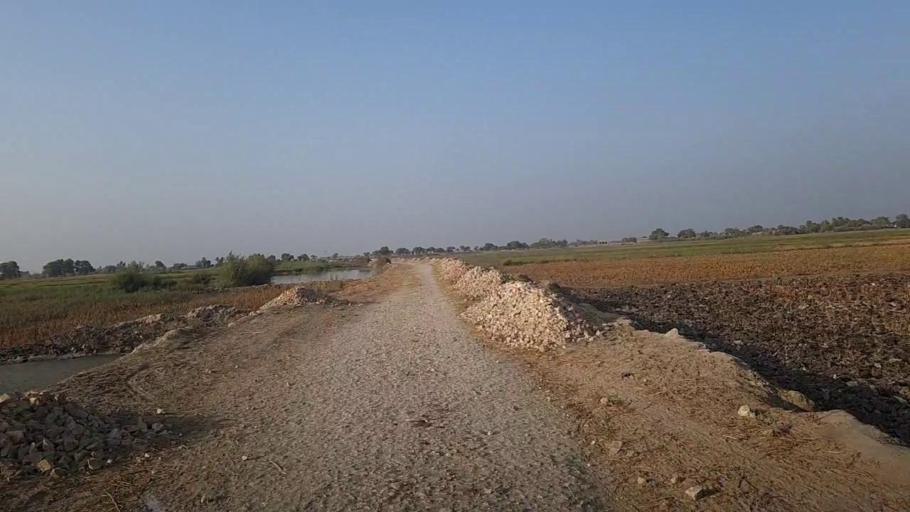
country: PK
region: Sindh
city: Tangwani
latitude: 28.2488
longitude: 69.0691
